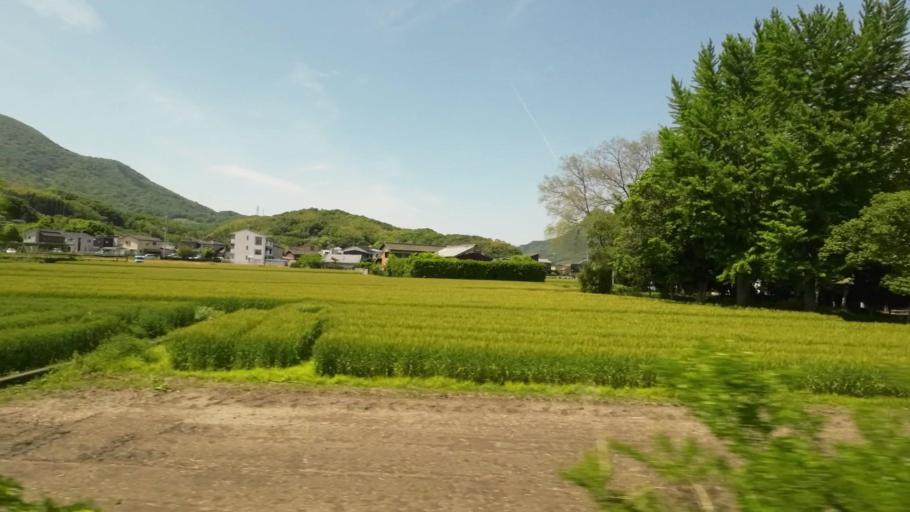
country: JP
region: Kagawa
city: Marugame
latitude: 34.2247
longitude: 133.7923
